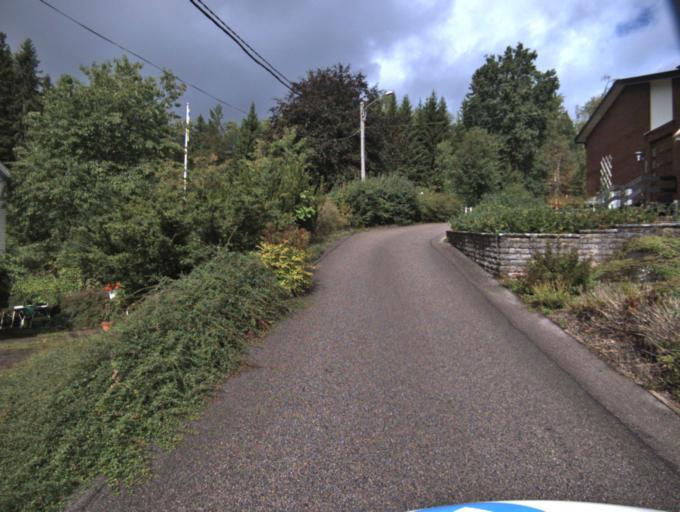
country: SE
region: Vaestra Goetaland
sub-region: Ulricehamns Kommun
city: Ulricehamn
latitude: 57.7265
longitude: 13.3086
